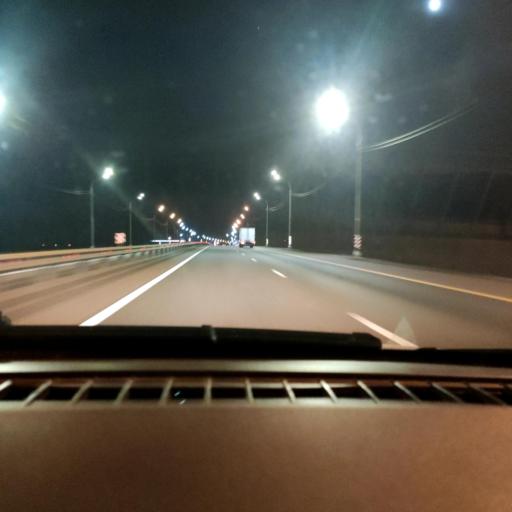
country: RU
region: Lipetsk
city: Khlevnoye
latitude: 52.2201
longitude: 39.1240
